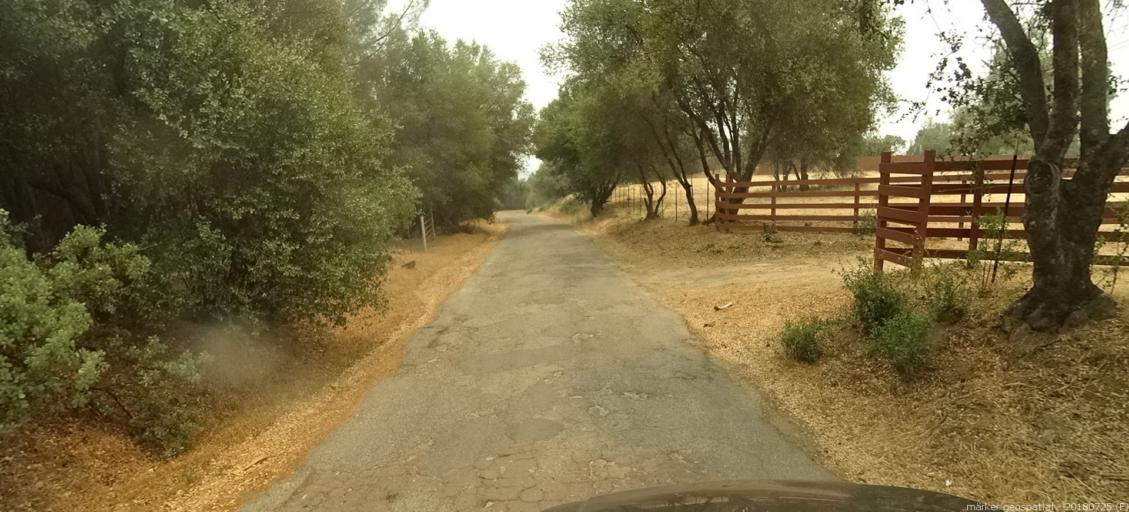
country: US
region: California
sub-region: Fresno County
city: Auberry
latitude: 37.2392
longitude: -119.5057
